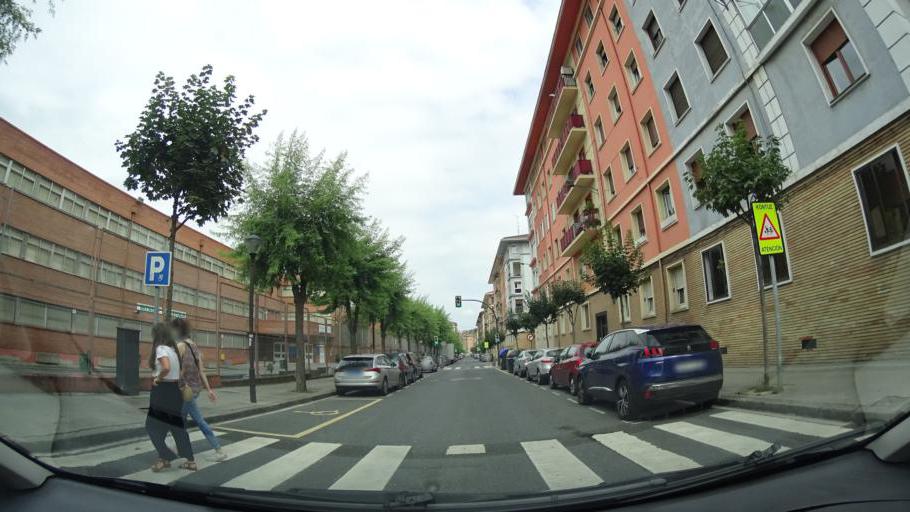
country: ES
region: Basque Country
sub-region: Bizkaia
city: Erandio
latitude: 43.2787
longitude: -2.9632
